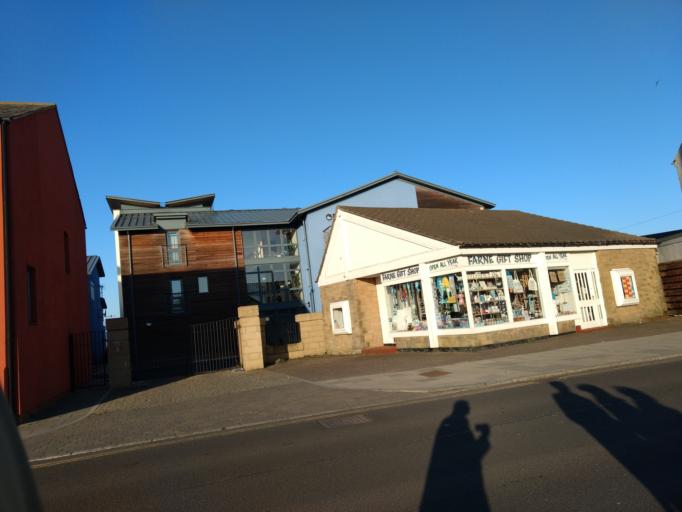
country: GB
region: England
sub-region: Northumberland
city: North Sunderland
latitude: 55.5823
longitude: -1.6541
